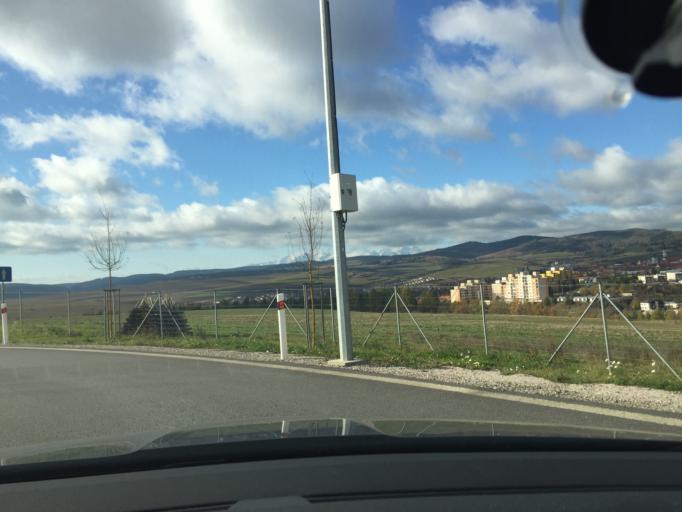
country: SK
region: Presovsky
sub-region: Okres Presov
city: Levoca
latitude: 49.0131
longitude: 20.6014
